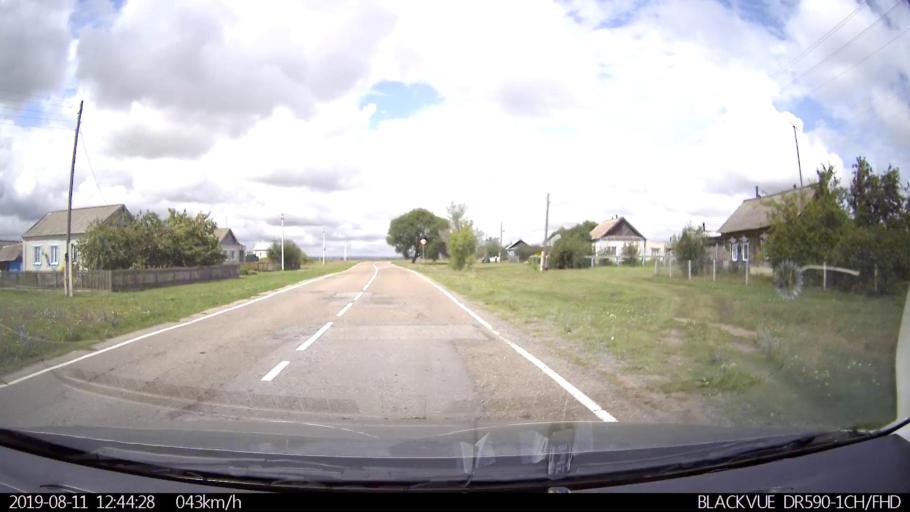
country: RU
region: Ulyanovsk
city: Ignatovka
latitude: 53.8550
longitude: 47.7359
